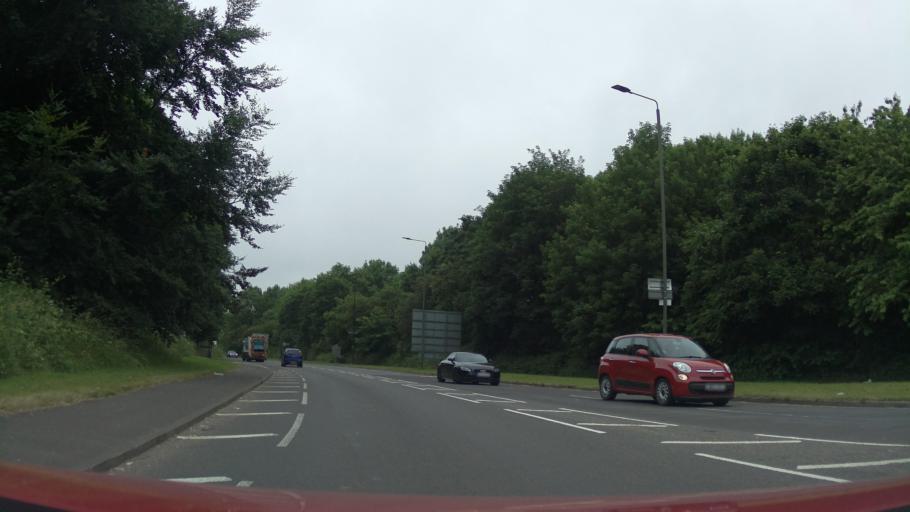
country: GB
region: England
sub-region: Derbyshire
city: Swadlincote
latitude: 52.7671
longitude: -1.5925
